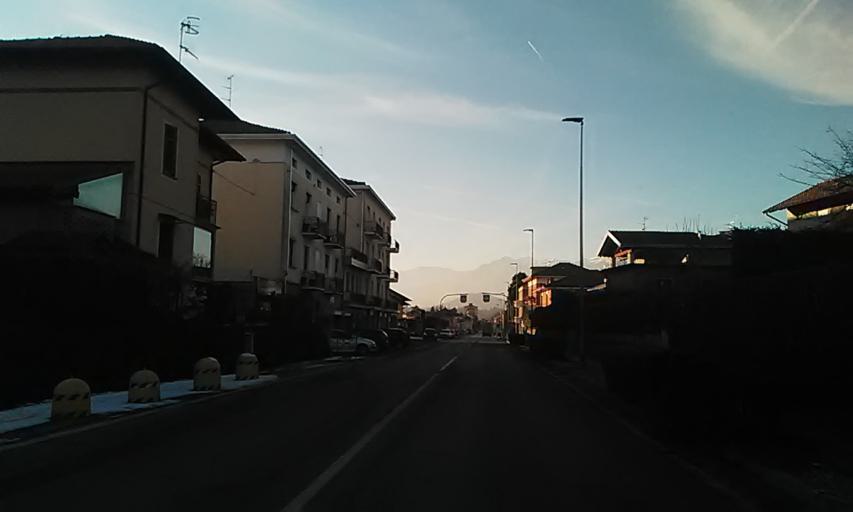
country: IT
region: Piedmont
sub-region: Provincia di Biella
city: Cossato
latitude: 45.5661
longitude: 8.1981
